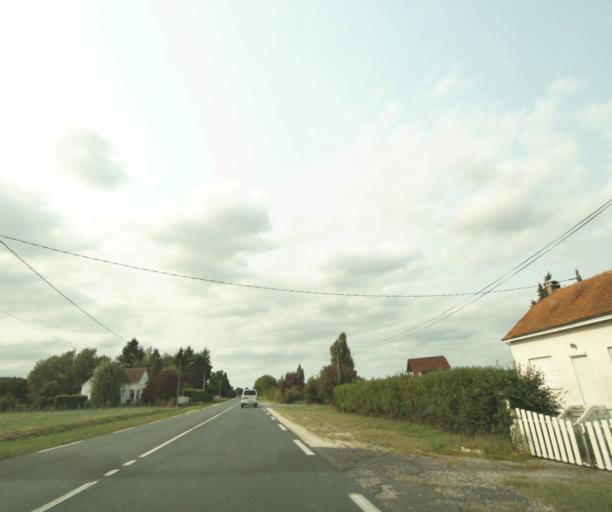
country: FR
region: Centre
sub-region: Departement de l'Indre
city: Chatillon-sur-Indre
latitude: 47.0241
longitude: 1.1038
